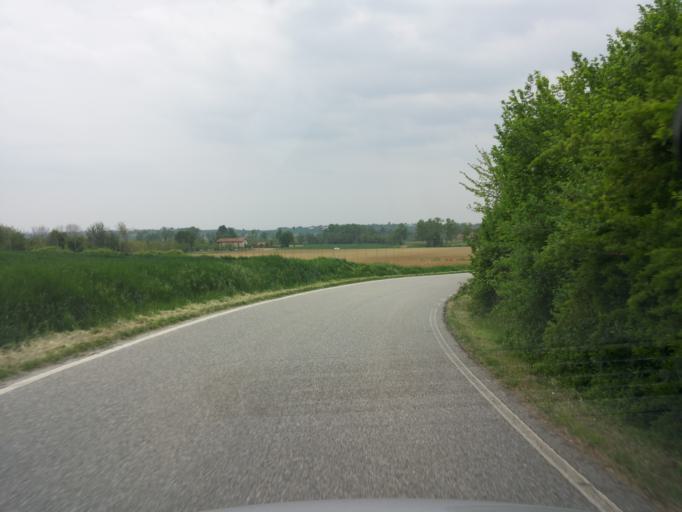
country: IT
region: Piedmont
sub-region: Provincia di Alessandria
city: Mirabello Monferrato
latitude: 45.0179
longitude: 8.5125
